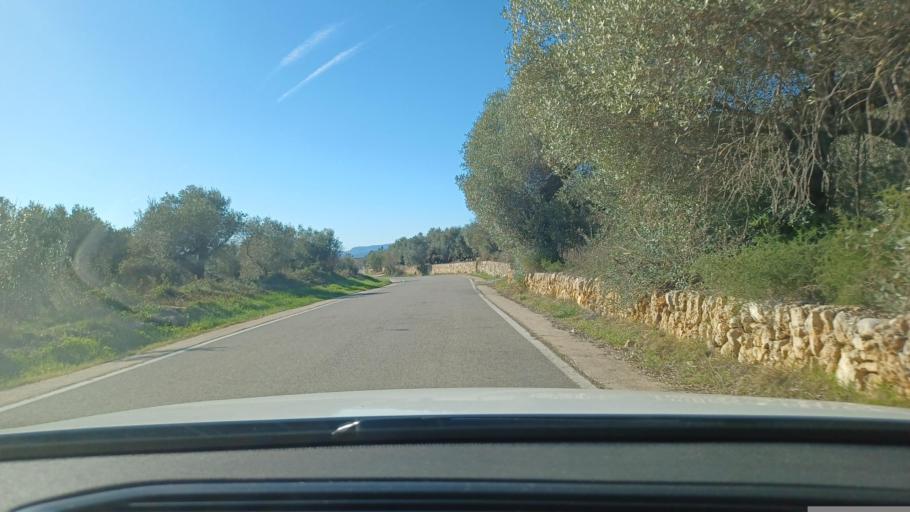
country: ES
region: Valencia
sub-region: Provincia de Castello
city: Rosell
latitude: 40.6351
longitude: 0.2971
